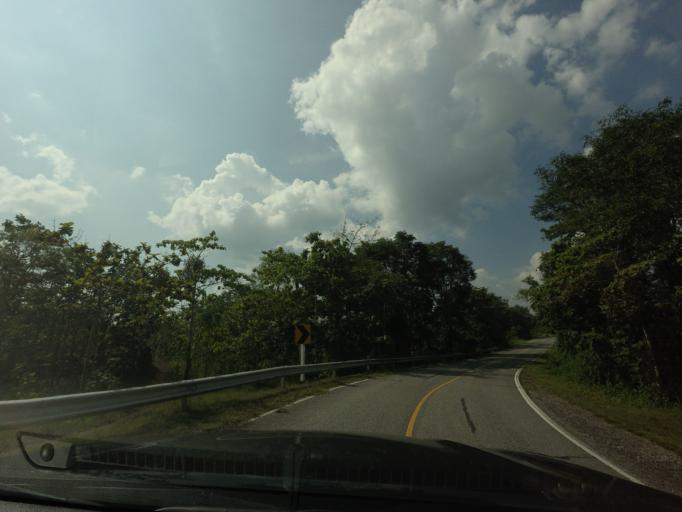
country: TH
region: Uttaradit
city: Ban Khok
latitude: 18.1679
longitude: 101.0798
